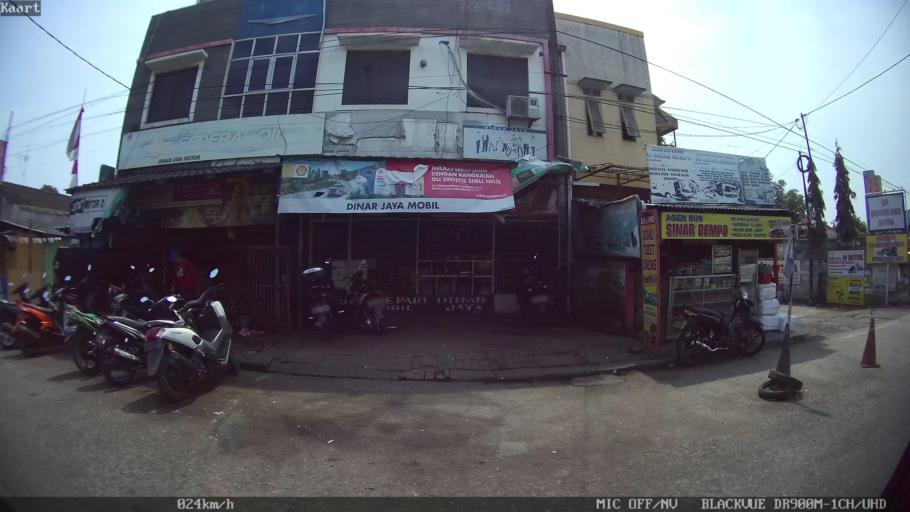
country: ID
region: Banten
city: Kubangkepuh
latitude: -5.9365
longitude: 106.0022
